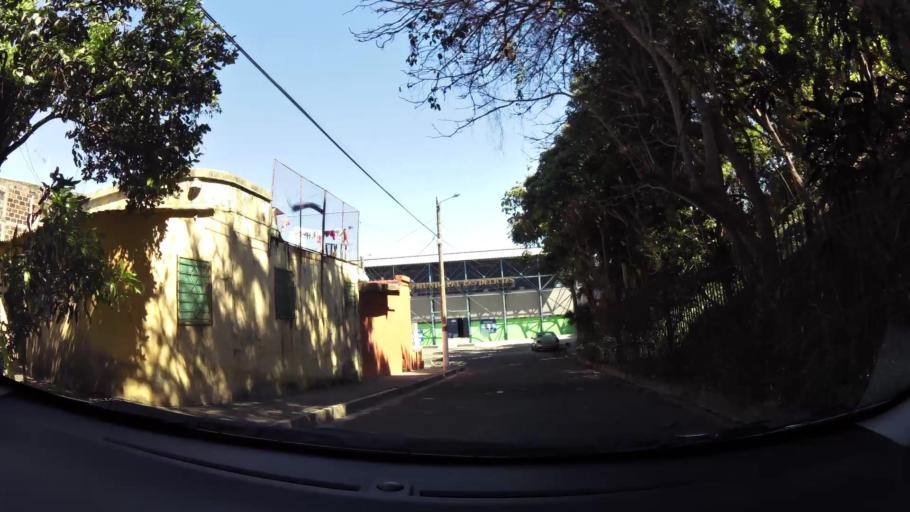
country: SV
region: La Libertad
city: Santa Tecla
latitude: 13.6716
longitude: -89.3005
